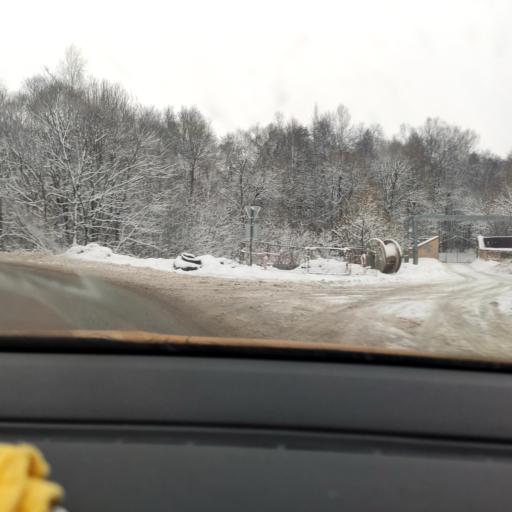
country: RU
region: Moskovskaya
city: Yershovo
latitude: 55.7622
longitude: 36.8665
